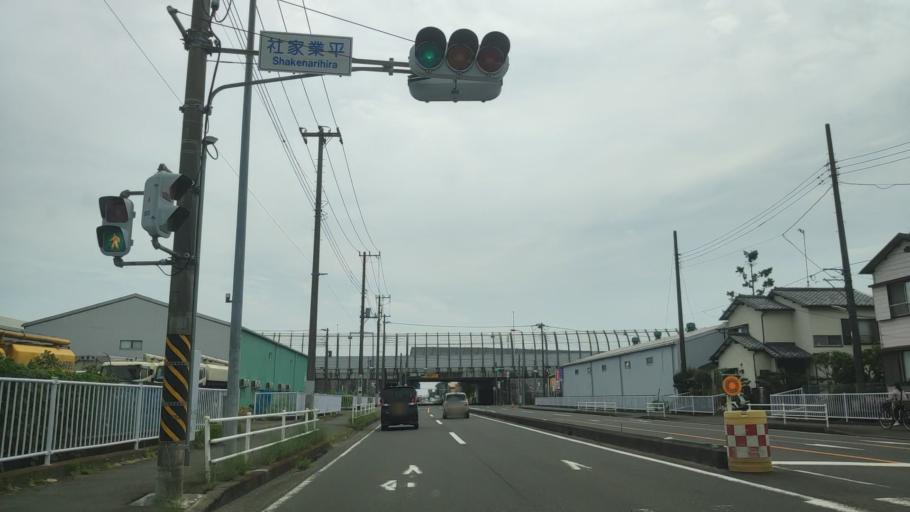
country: JP
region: Kanagawa
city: Atsugi
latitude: 35.4243
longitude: 139.3818
